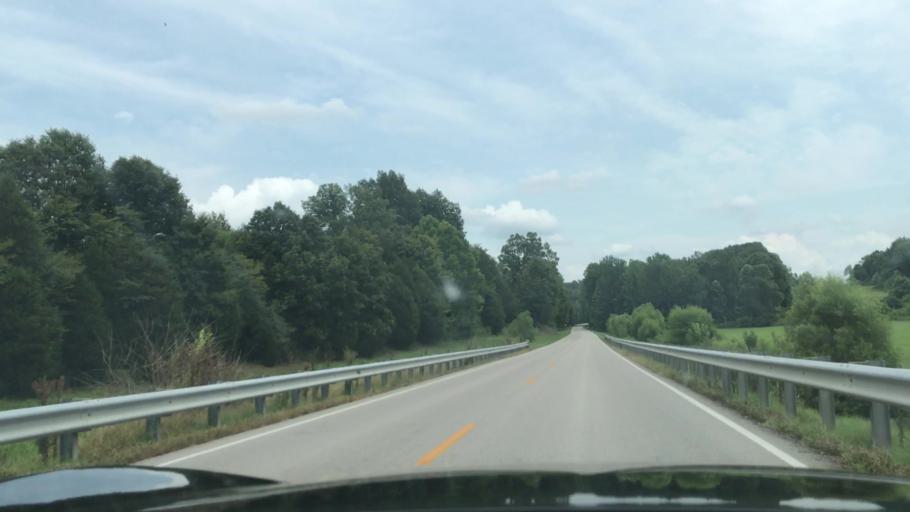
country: US
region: Kentucky
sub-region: Butler County
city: Morgantown
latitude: 37.1762
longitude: -86.8467
